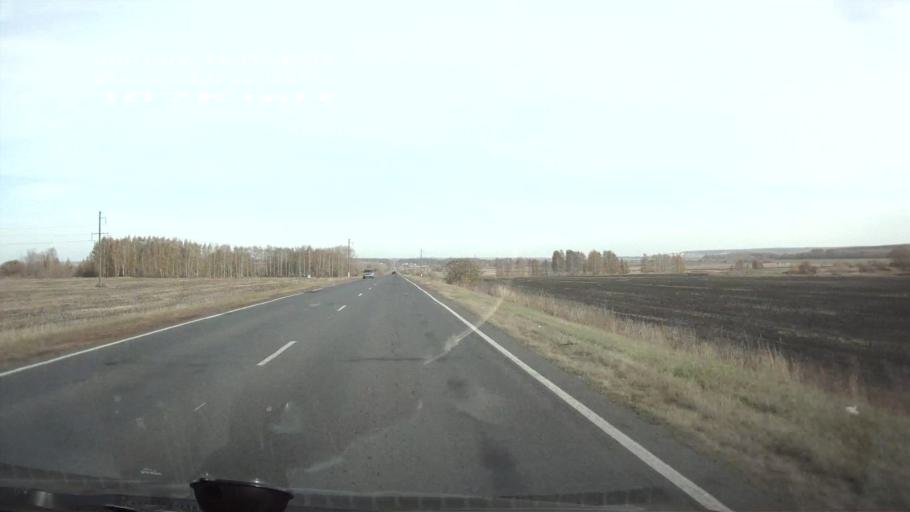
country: RU
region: Mordoviya
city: Atyashevo
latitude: 54.5429
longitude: 45.9394
